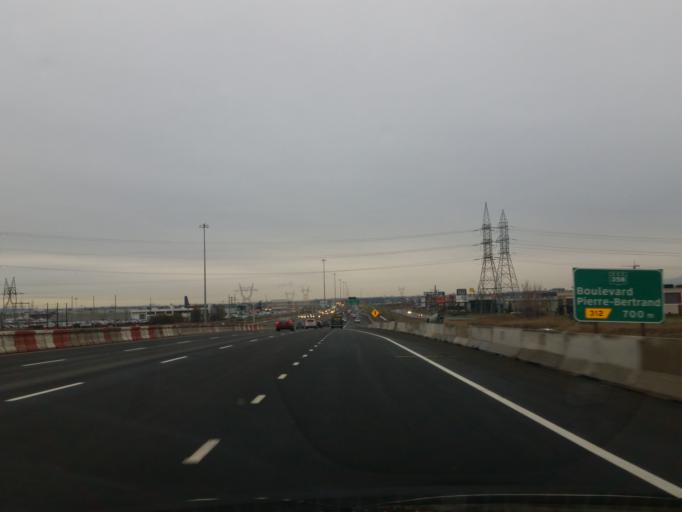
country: CA
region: Quebec
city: Quebec
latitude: 46.8366
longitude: -71.2658
